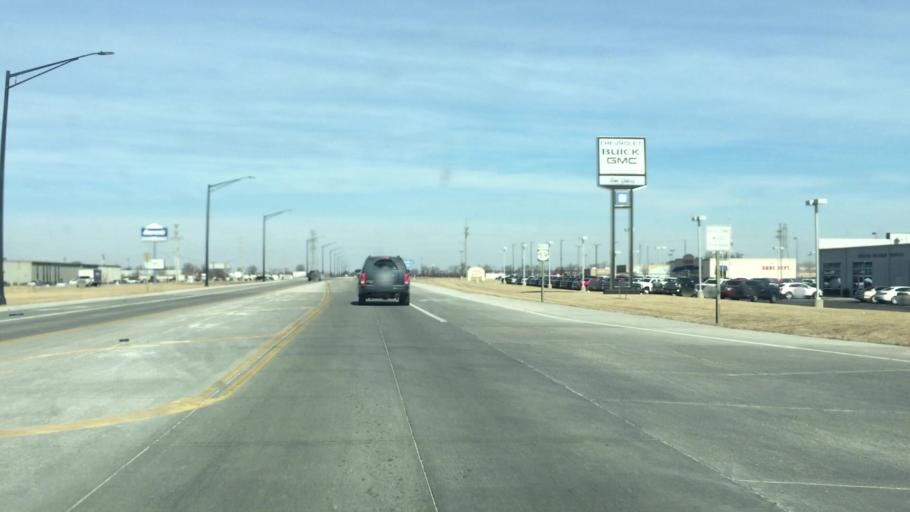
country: US
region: Kansas
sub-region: Labette County
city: Parsons
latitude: 37.3678
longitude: -95.2585
